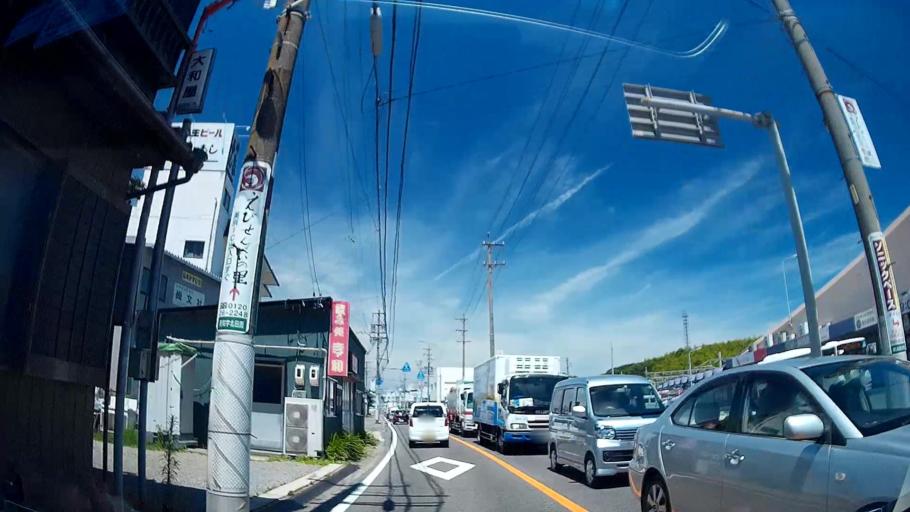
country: JP
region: Aichi
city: Toyohama
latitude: 34.7776
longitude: 136.9121
